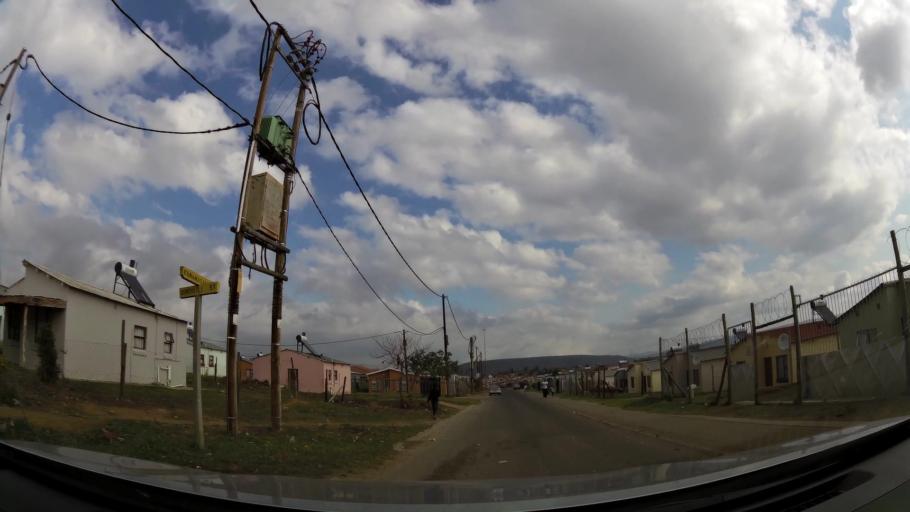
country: ZA
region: Eastern Cape
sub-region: Nelson Mandela Bay Metropolitan Municipality
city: Uitenhage
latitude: -33.7464
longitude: 25.3942
